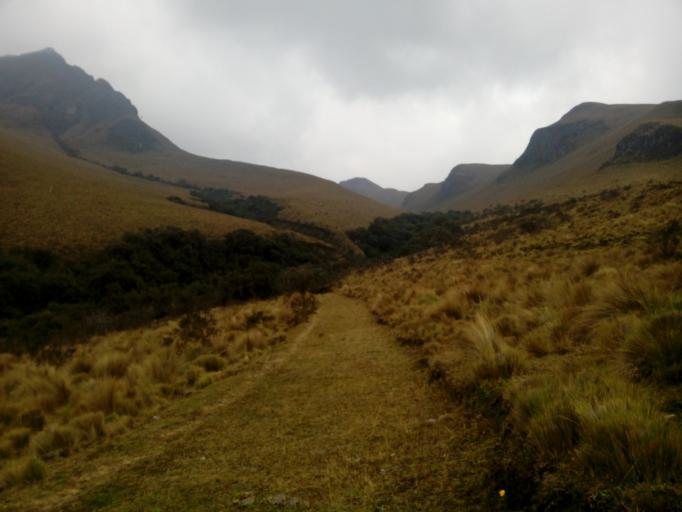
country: EC
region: Pichincha
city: Machachi
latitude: -0.5601
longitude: -78.5271
